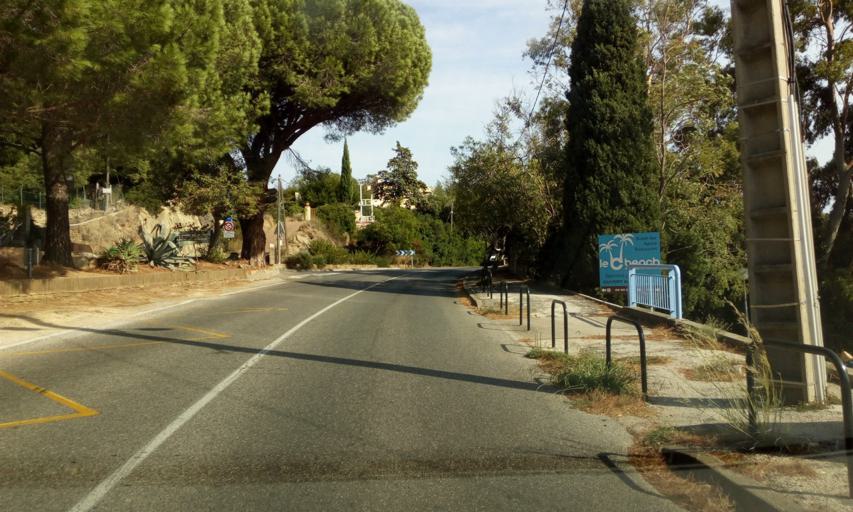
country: FR
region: Provence-Alpes-Cote d'Azur
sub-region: Departement du Var
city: Le Lavandou
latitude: 43.1463
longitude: 6.3955
